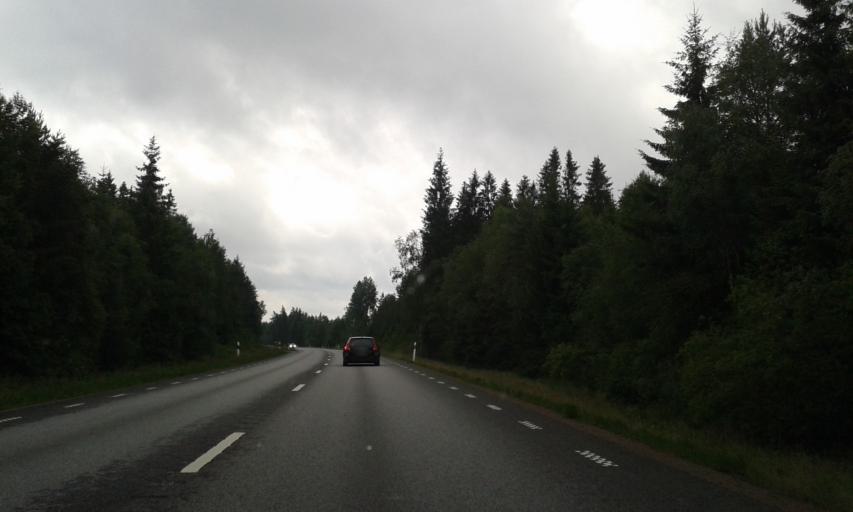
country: SE
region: Joenkoeping
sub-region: Gislaveds Kommun
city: Gislaved
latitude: 57.3512
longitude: 13.4885
